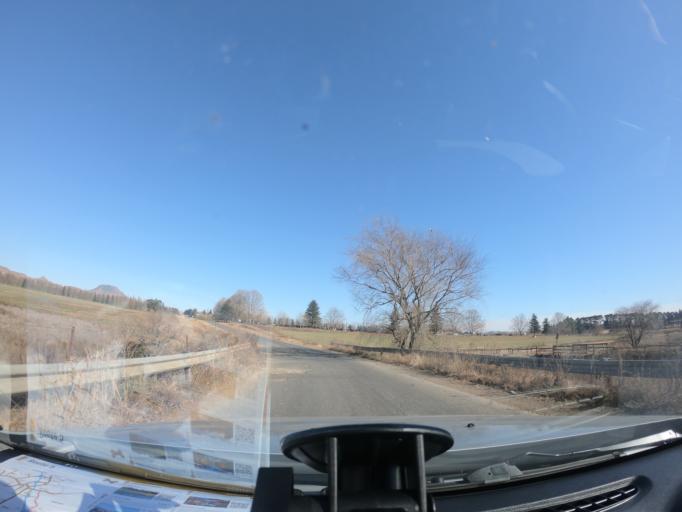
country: ZA
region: KwaZulu-Natal
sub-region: uMgungundlovu District Municipality
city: Mooirivier
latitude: -29.3243
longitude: 29.8334
